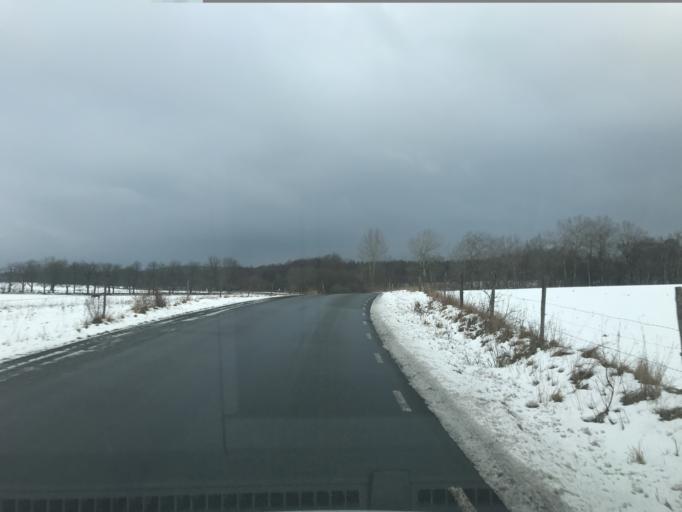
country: SE
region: Skane
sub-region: Kristianstads Kommun
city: Degeberga
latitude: 55.7469
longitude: 13.9422
